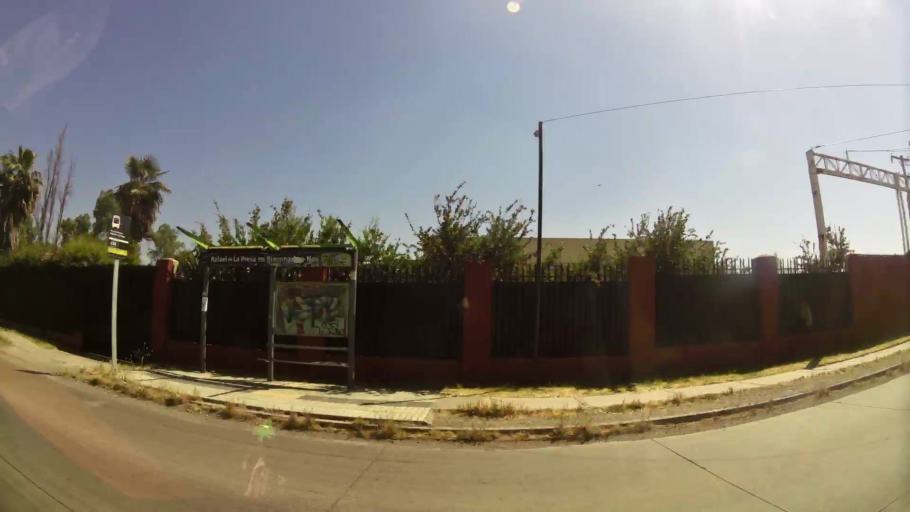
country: CL
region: Santiago Metropolitan
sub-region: Provincia de Maipo
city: San Bernardo
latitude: -33.6238
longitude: -70.6969
